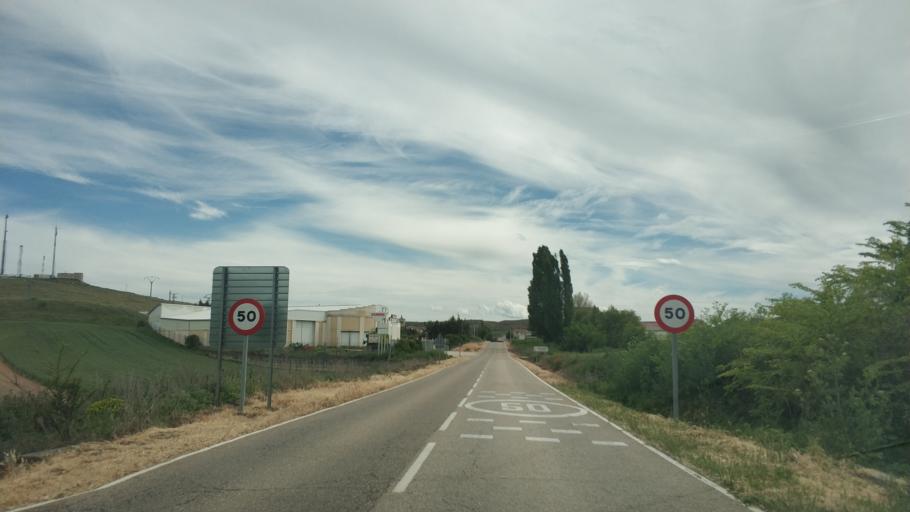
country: ES
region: Castille and Leon
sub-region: Provincia de Soria
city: Berlanga de Duero
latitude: 41.4732
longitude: -2.8614
